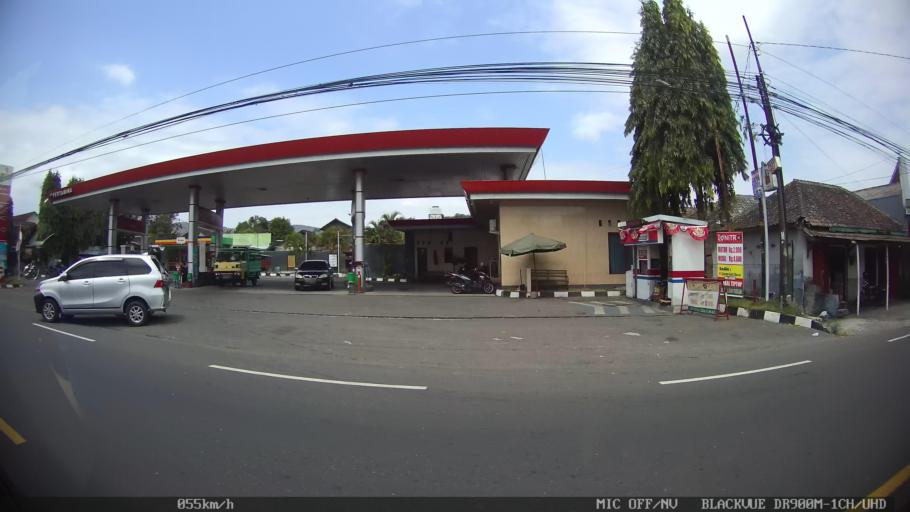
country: ID
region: Daerah Istimewa Yogyakarta
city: Depok
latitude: -7.8319
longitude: 110.4608
